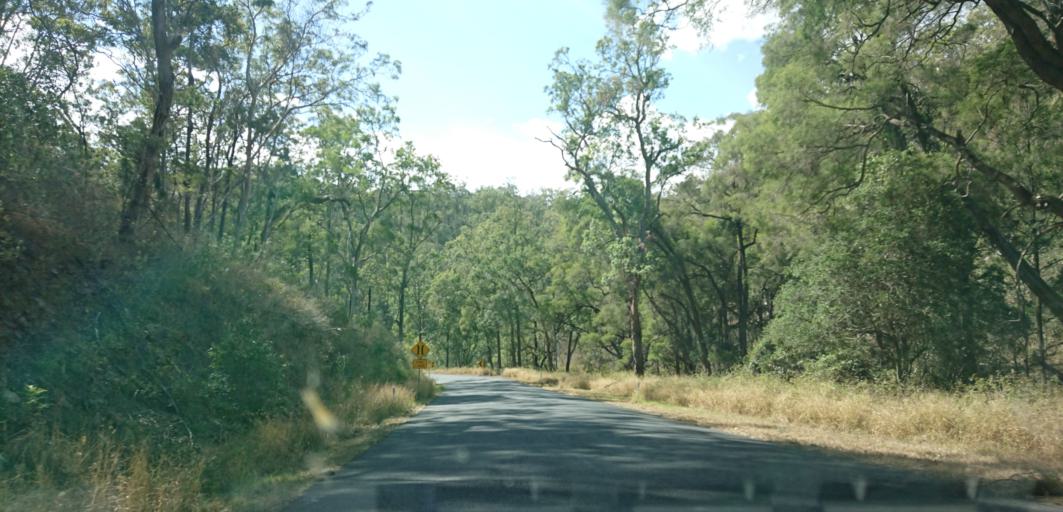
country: AU
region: Queensland
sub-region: Toowoomba
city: Top Camp
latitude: -27.7736
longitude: 152.0906
